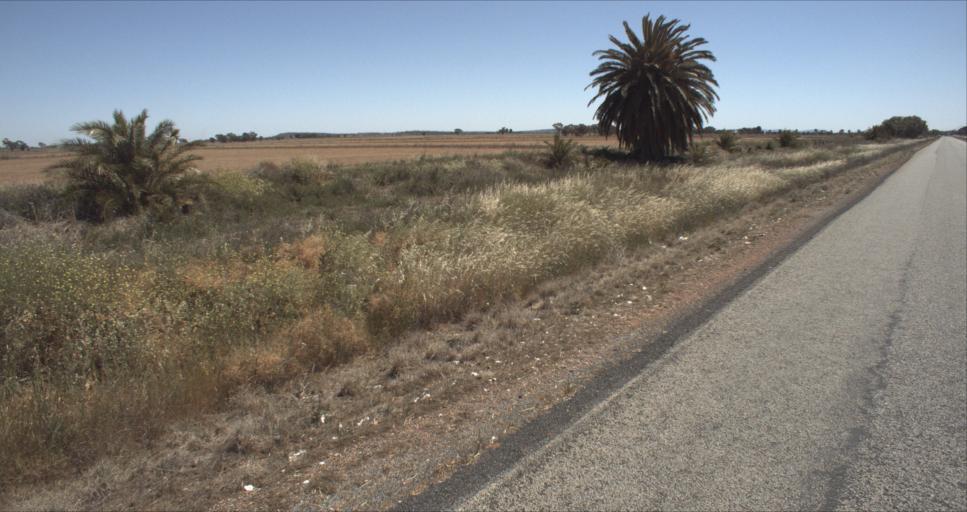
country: AU
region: New South Wales
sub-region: Leeton
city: Leeton
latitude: -34.4520
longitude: 146.2958
